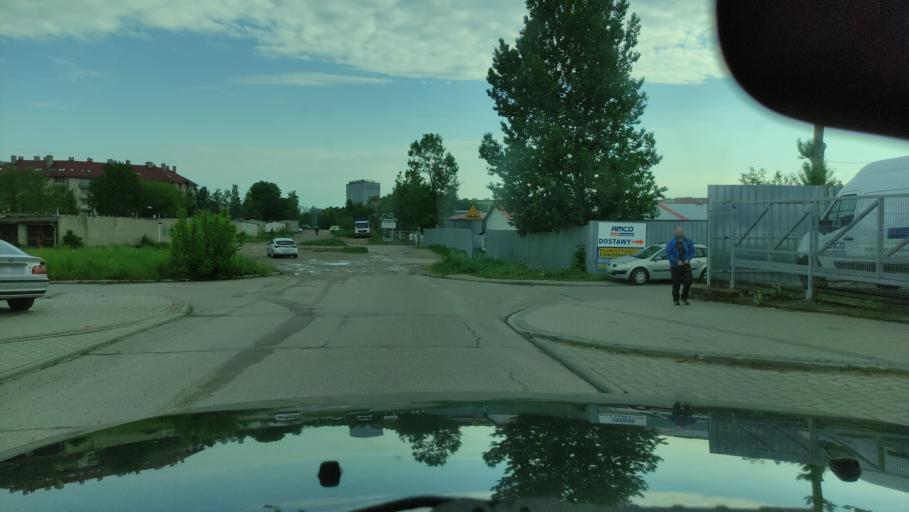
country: PL
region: Warmian-Masurian Voivodeship
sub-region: Powiat olsztynski
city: Olsztyn
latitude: 53.7669
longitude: 20.5100
